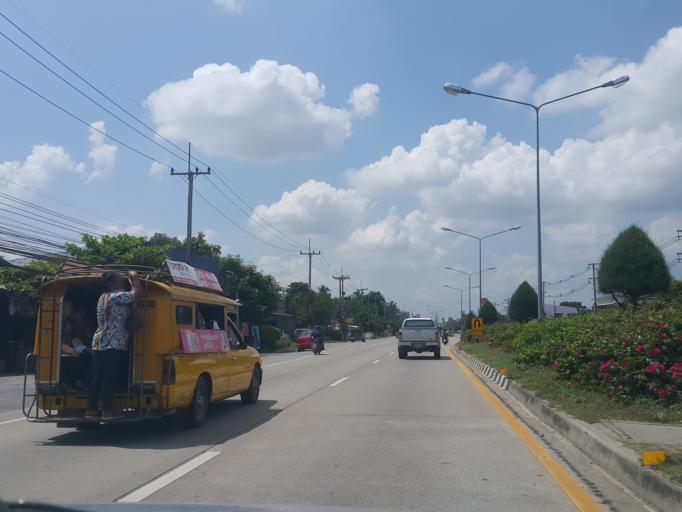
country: TH
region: Chiang Mai
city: San Sai
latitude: 18.8200
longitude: 99.0400
